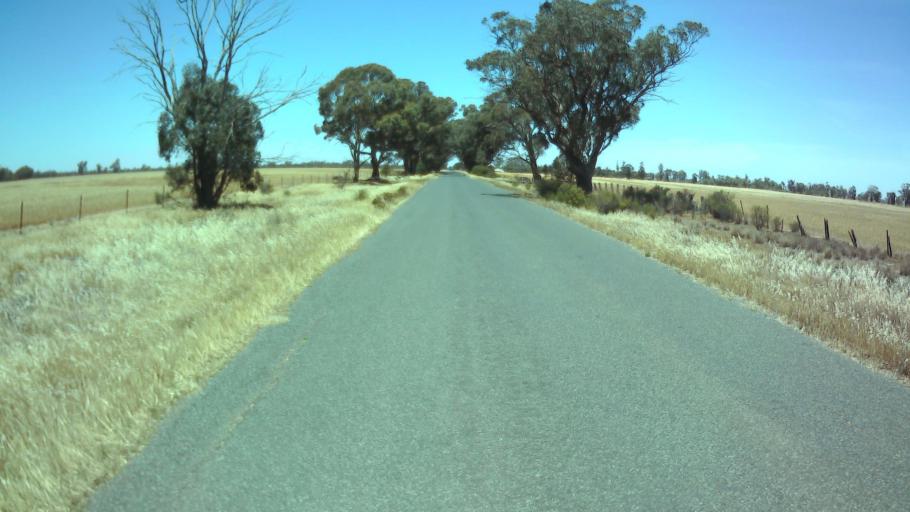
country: AU
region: New South Wales
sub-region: Weddin
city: Grenfell
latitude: -34.0208
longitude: 147.7926
